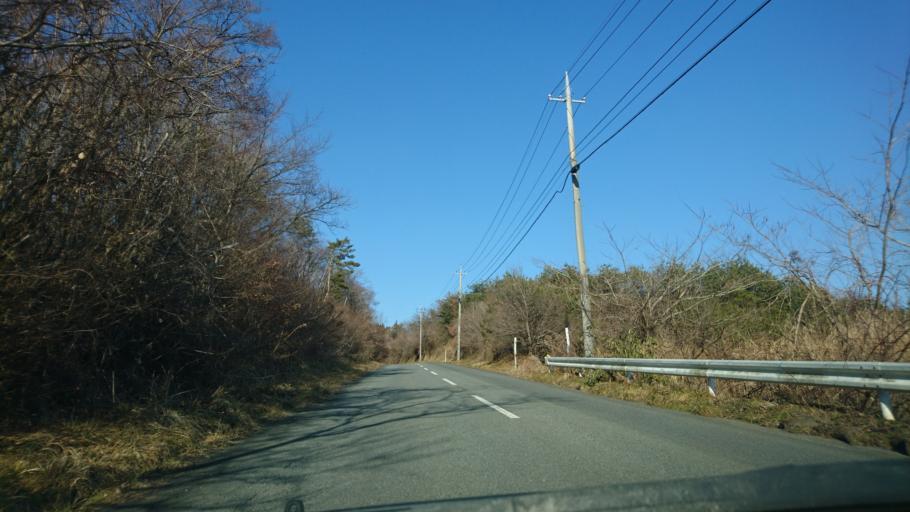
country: JP
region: Iwate
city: Ichinoseki
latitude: 38.8244
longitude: 141.2817
